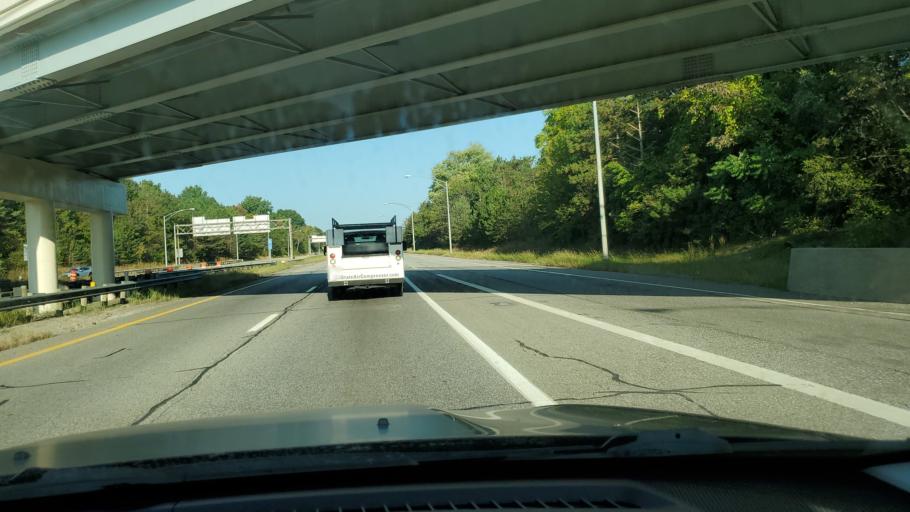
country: US
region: Ohio
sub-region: Trumbull County
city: Girard
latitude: 41.1192
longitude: -80.6969
